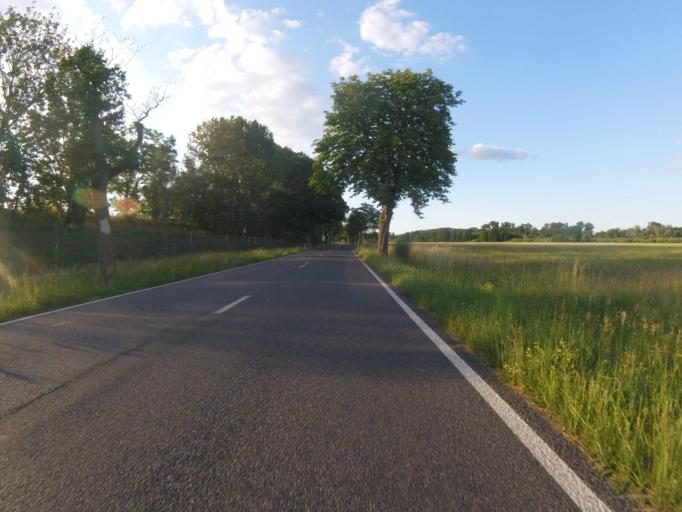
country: DE
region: Brandenburg
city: Mittenwalde
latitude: 52.2300
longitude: 13.5490
